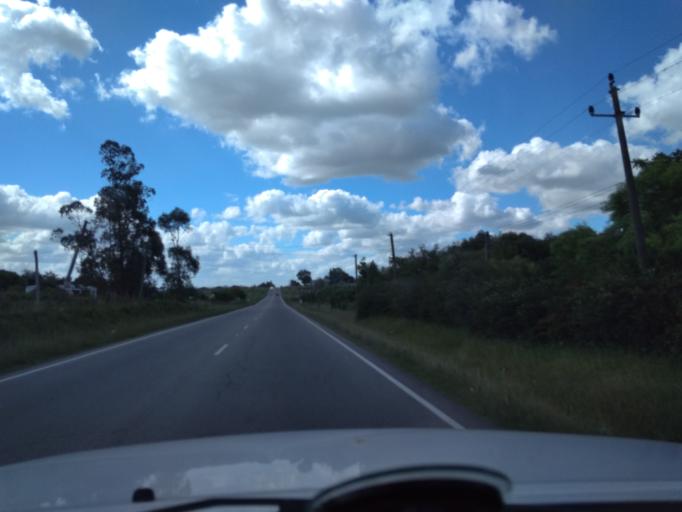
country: UY
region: Canelones
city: Joaquin Suarez
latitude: -34.7068
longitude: -56.0584
